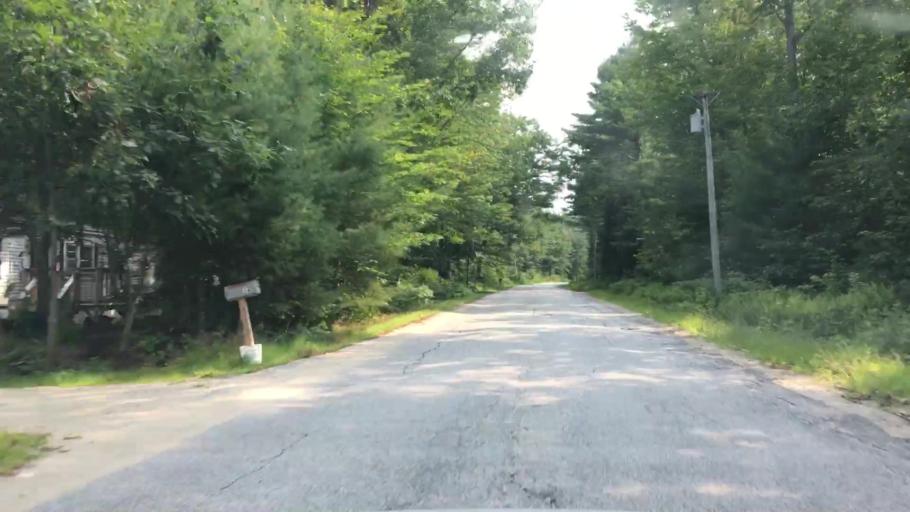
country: US
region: Maine
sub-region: Androscoggin County
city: Livermore
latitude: 44.3335
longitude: -70.2909
